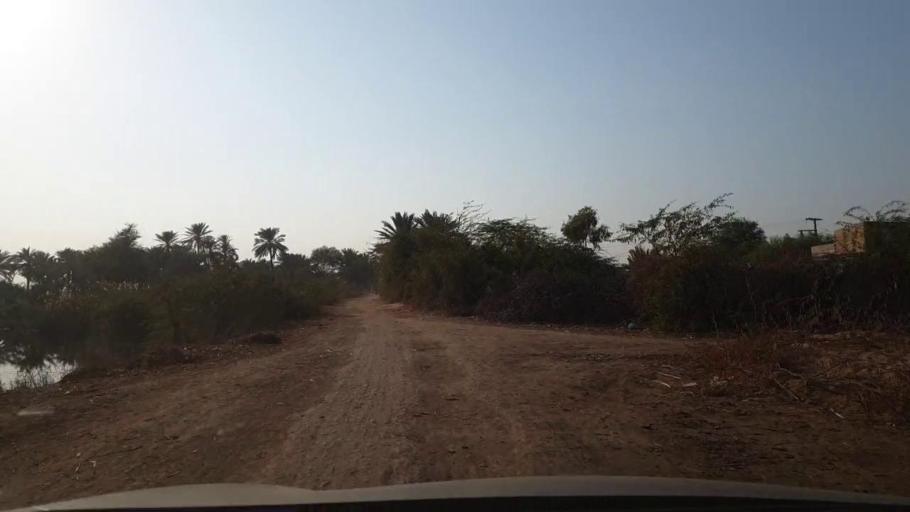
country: PK
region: Sindh
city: Berani
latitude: 25.6543
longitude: 68.8240
